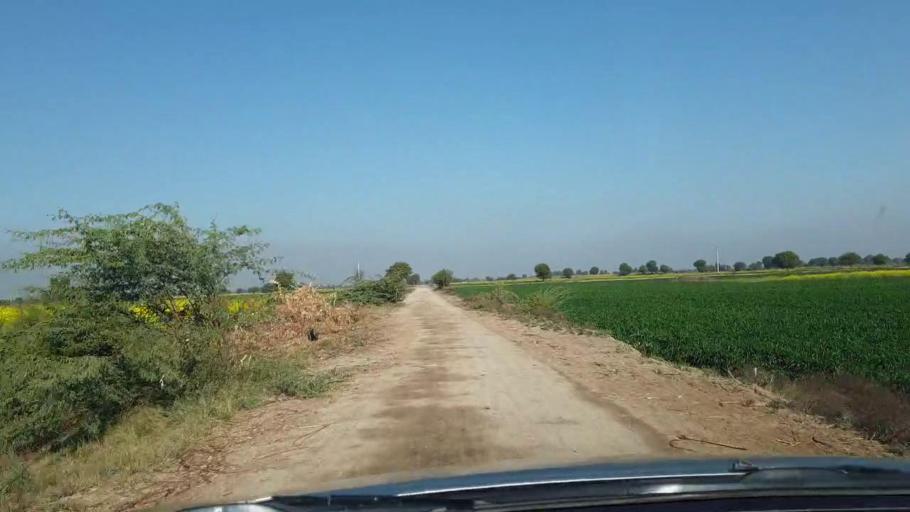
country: PK
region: Sindh
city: Jhol
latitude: 25.8903
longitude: 68.9054
